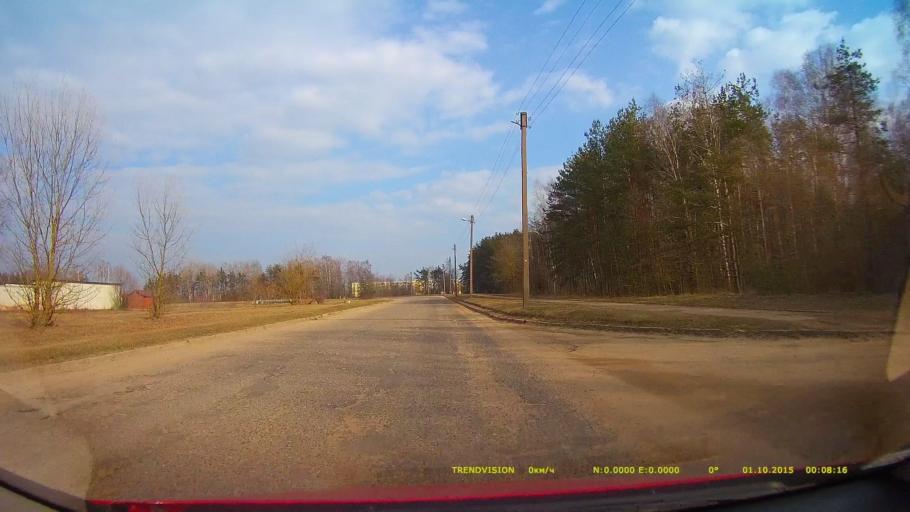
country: BY
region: Grodnenskaya
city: Lida
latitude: 53.9351
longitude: 25.2565
